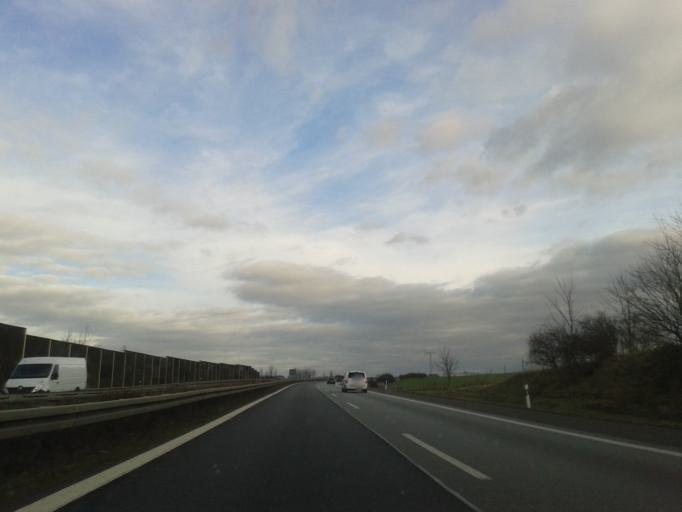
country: DE
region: Saxony
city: Bautzen
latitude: 51.1947
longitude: 14.4212
